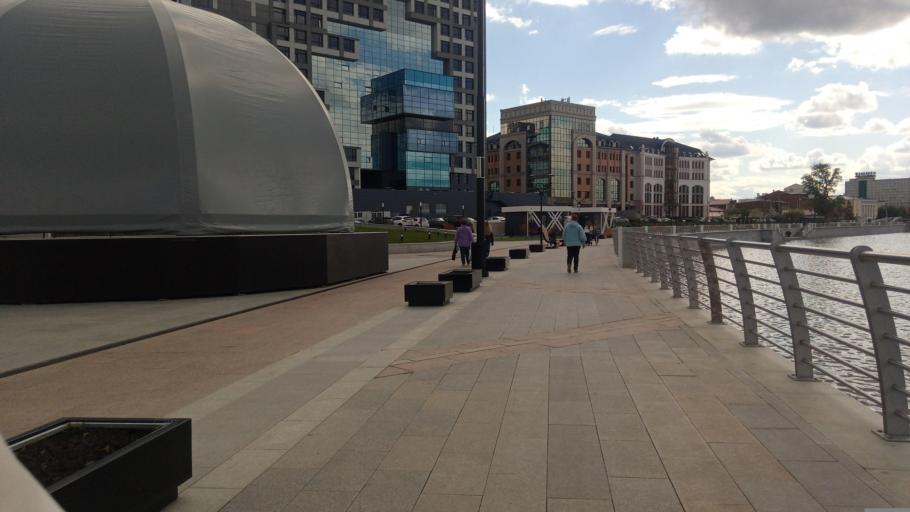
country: RU
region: Chelyabinsk
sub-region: Gorod Chelyabinsk
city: Chelyabinsk
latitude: 55.1698
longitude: 61.4077
